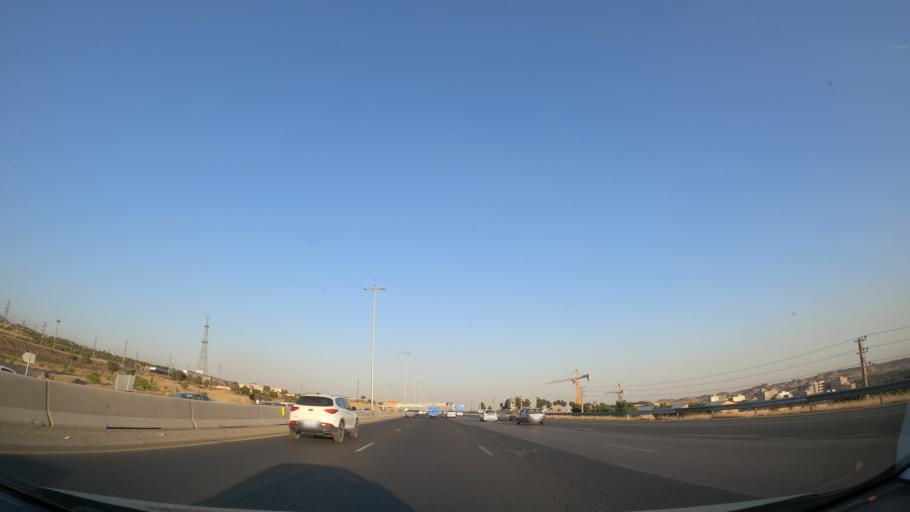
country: IR
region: Tehran
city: Shahr-e Qods
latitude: 35.7524
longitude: 51.0773
